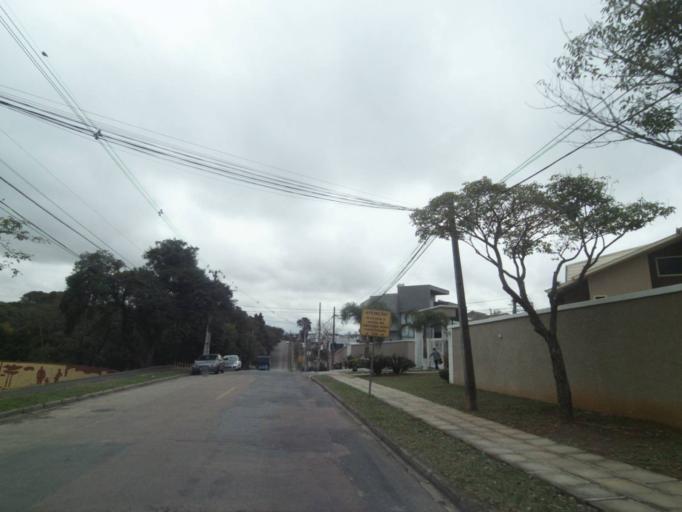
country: BR
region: Parana
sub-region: Curitiba
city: Curitiba
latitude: -25.5072
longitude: -49.2905
